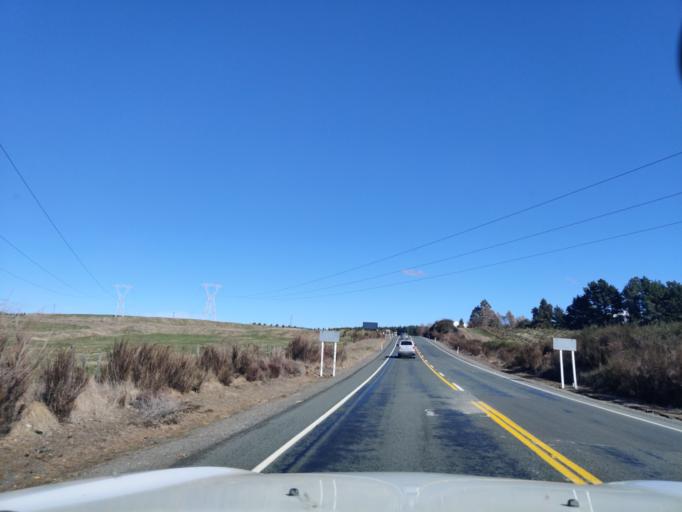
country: NZ
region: Waikato
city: Turangi
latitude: -39.0726
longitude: 175.8122
